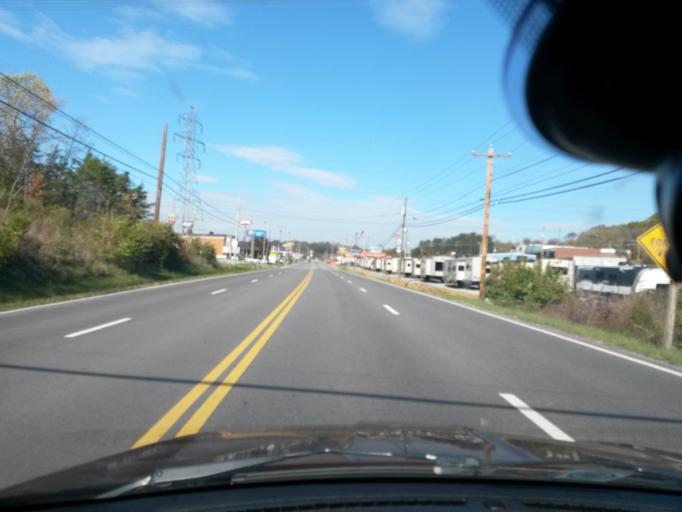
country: US
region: Virginia
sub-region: Botetourt County
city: Cloverdale
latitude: 37.3818
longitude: -79.9028
